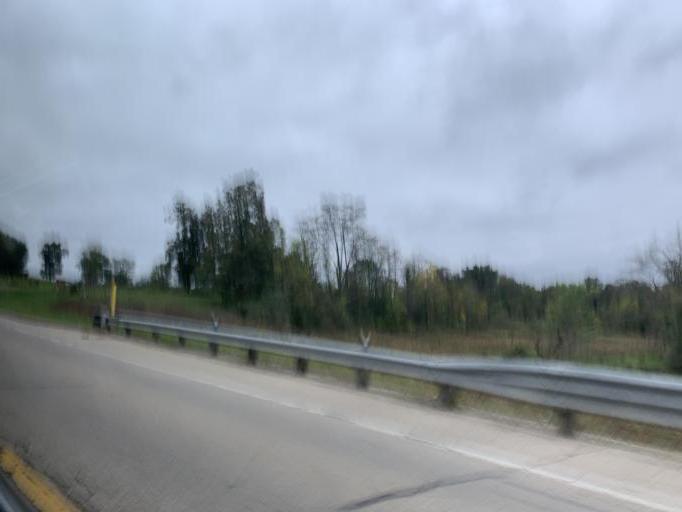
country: US
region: Wisconsin
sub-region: Grant County
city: Muscoda
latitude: 43.2198
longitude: -90.5458
